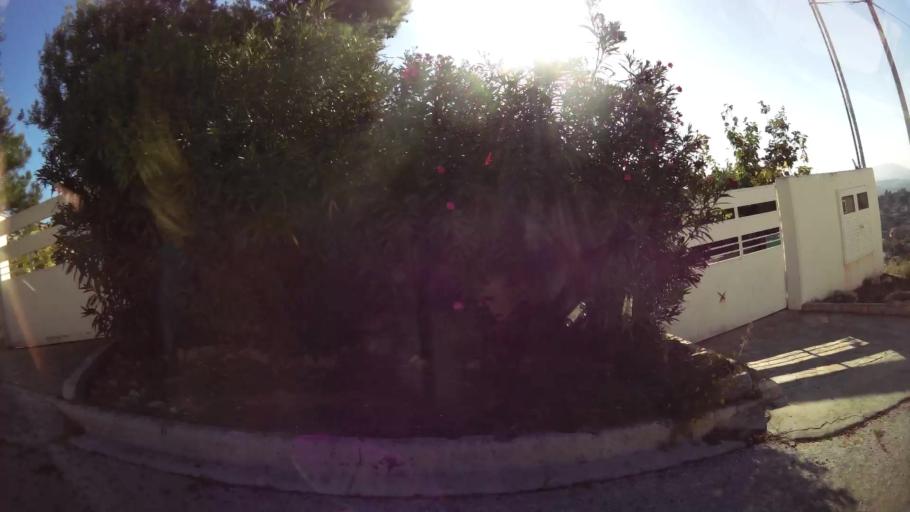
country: GR
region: Attica
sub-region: Nomarchia Anatolikis Attikis
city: Dhrafi
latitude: 38.0237
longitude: 23.9049
